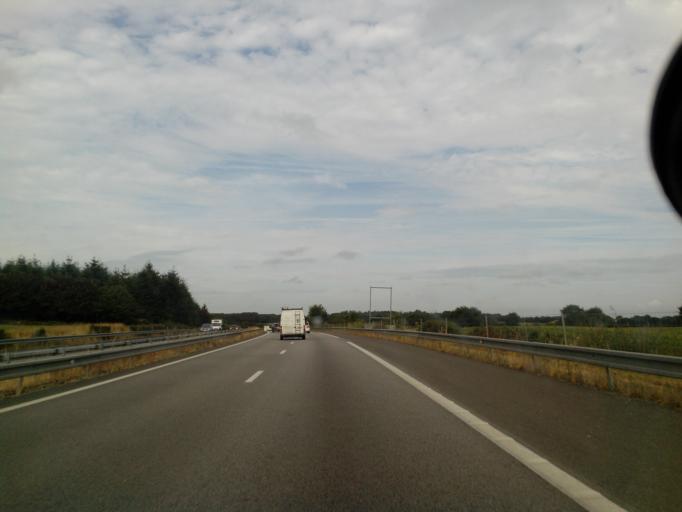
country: FR
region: Brittany
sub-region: Departement du Morbihan
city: Ambon
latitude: 47.5919
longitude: -2.5574
